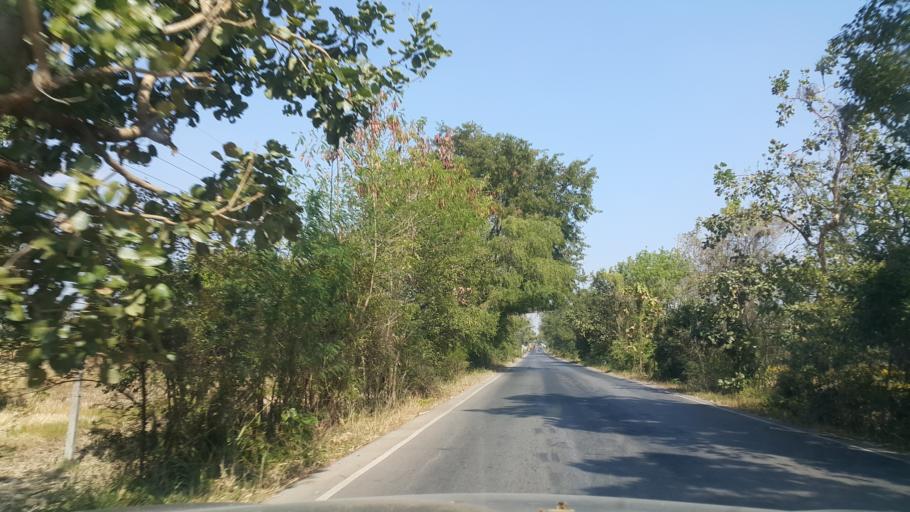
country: TH
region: Chaiyaphum
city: Khon Sawan
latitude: 15.8824
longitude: 102.2374
